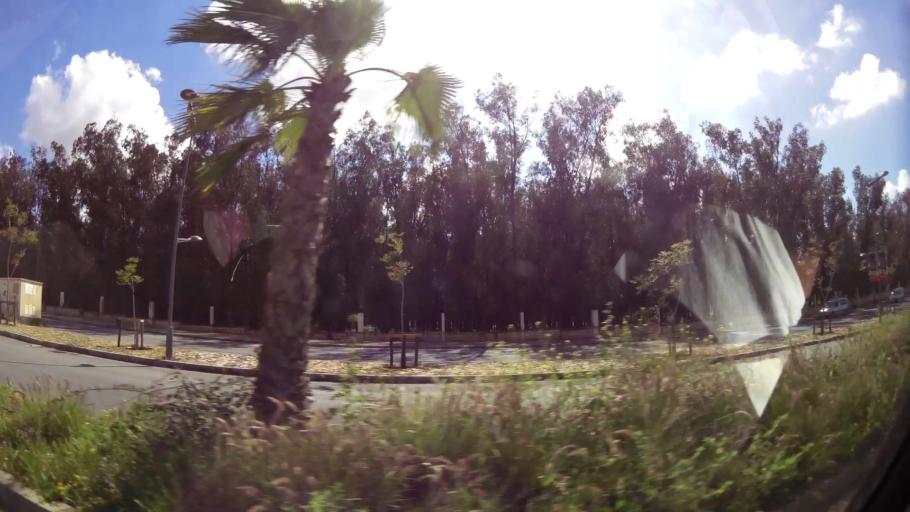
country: MA
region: Grand Casablanca
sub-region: Nouaceur
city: Bouskoura
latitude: 33.4738
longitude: -7.6170
